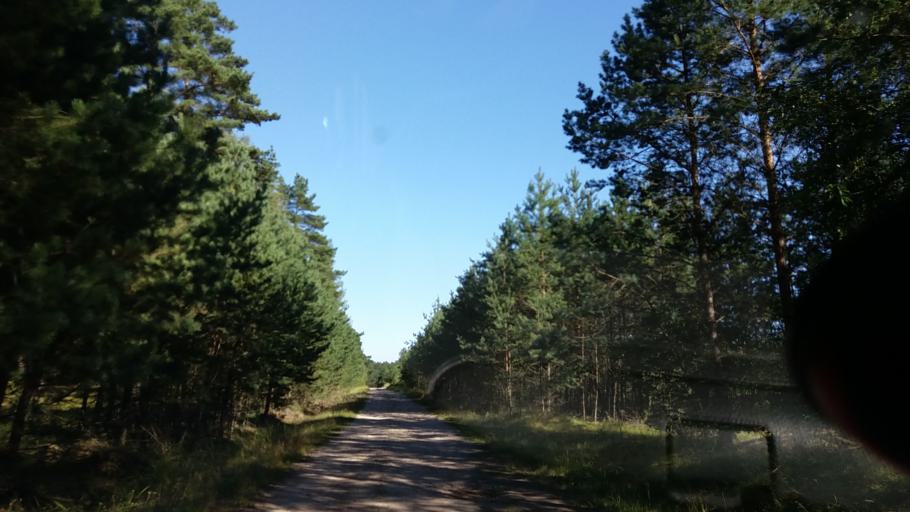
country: PL
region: West Pomeranian Voivodeship
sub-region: Powiat szczecinecki
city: Borne Sulinowo
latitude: 53.5557
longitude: 16.5079
